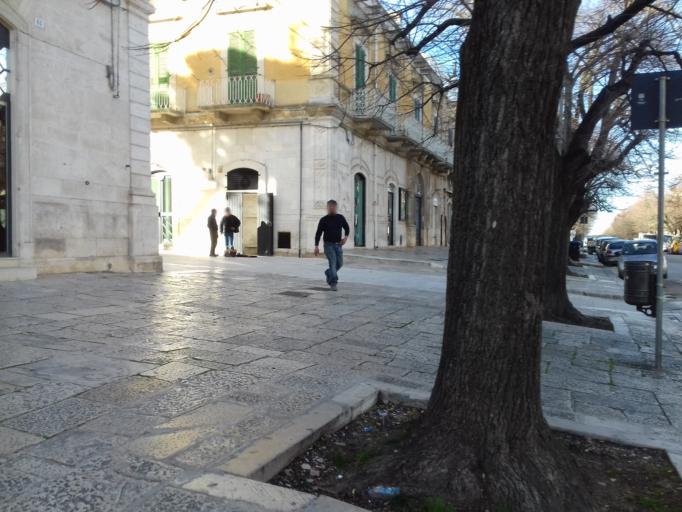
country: IT
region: Apulia
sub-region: Provincia di Bari
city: Ruvo di Puglia
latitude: 41.1167
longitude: 16.4878
